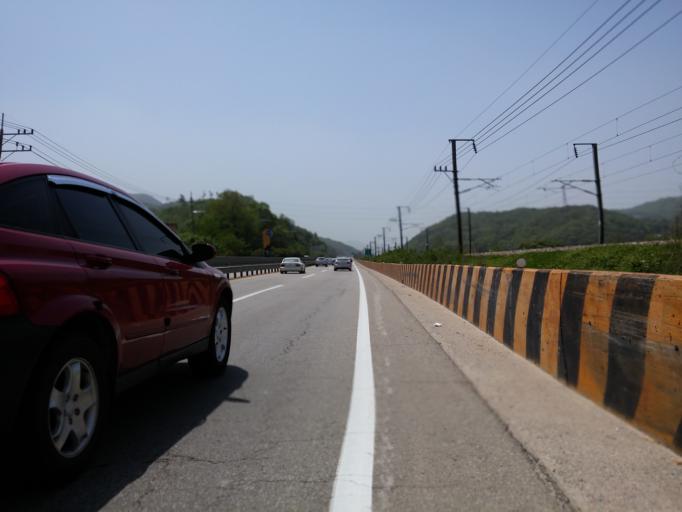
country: KR
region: Chungcheongnam-do
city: Nonsan
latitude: 36.2612
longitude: 127.2286
